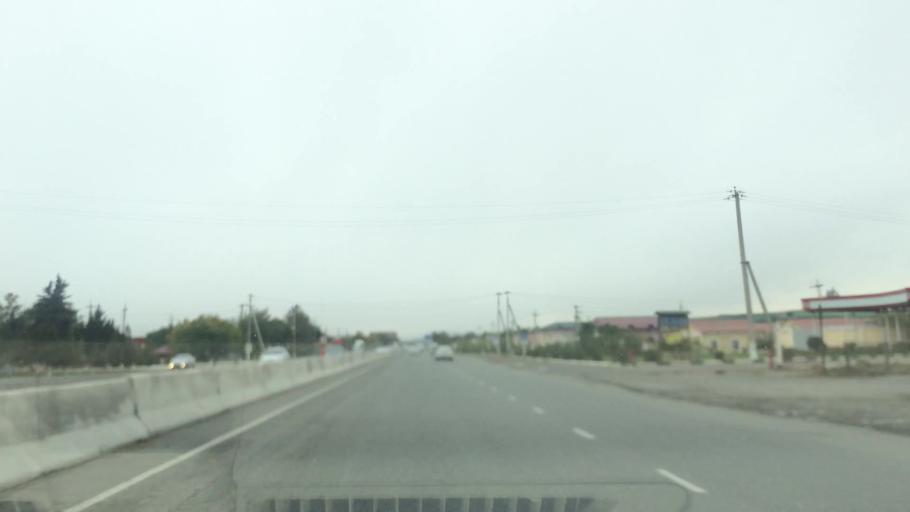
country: UZ
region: Samarqand
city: Jomboy
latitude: 39.7027
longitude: 67.0785
